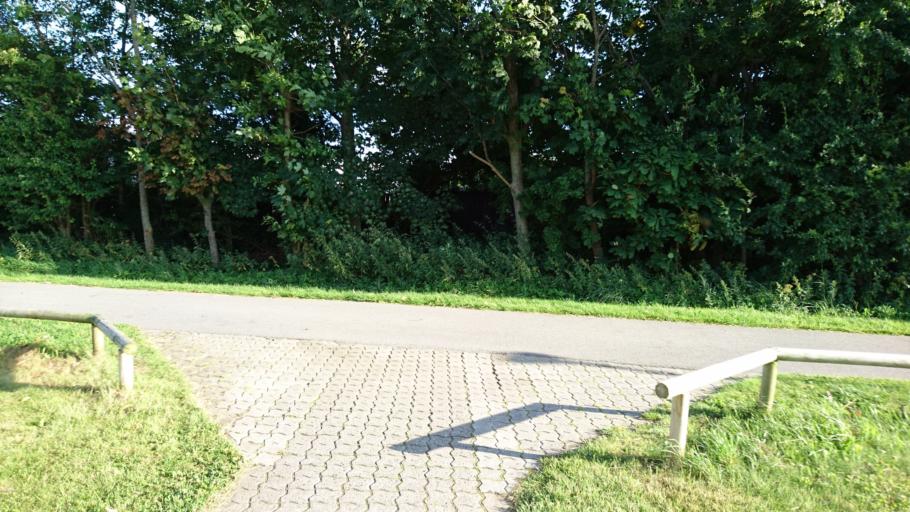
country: DK
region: North Denmark
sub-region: Frederikshavn Kommune
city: Skagen
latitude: 57.7314
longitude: 10.5919
